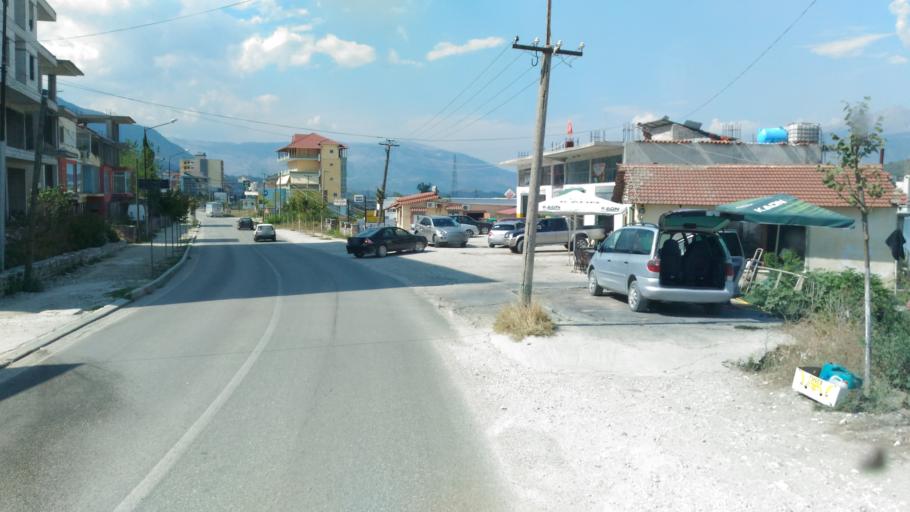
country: AL
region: Gjirokaster
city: Gjirokaster
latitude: 40.0755
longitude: 20.1538
